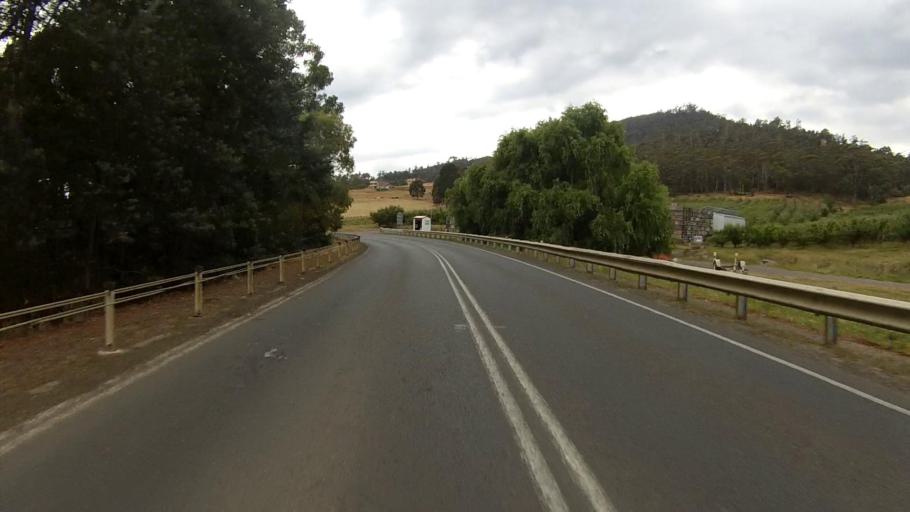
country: AU
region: Tasmania
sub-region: Huon Valley
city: Franklin
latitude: -43.0888
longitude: 147.0285
